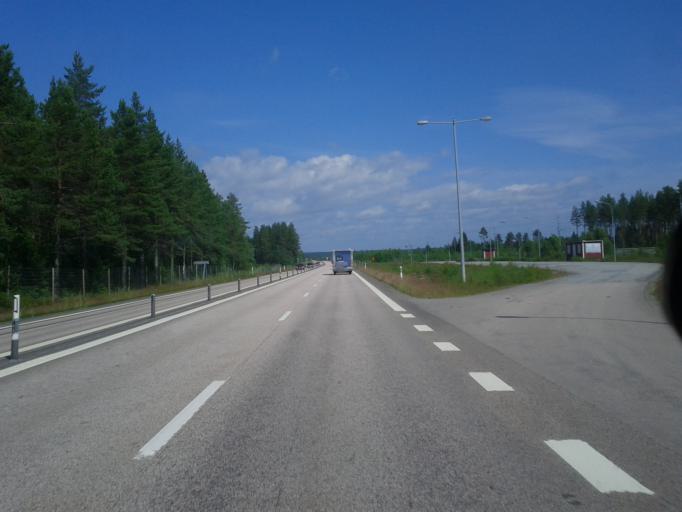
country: SE
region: Vaesterbotten
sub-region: Nordmalings Kommun
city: Nordmaling
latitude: 63.5538
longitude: 19.4197
